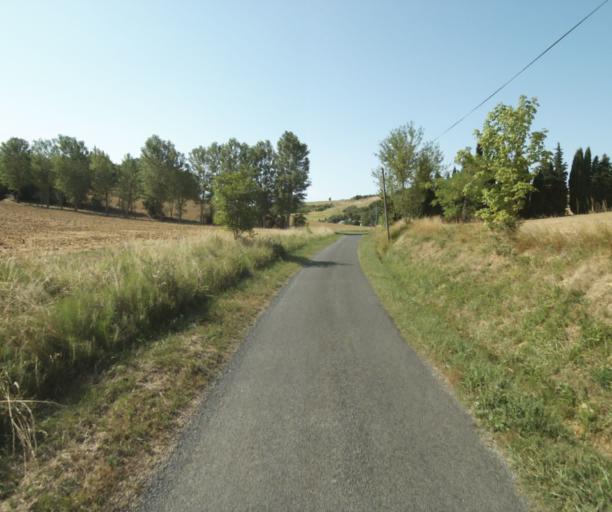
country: FR
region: Midi-Pyrenees
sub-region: Departement de la Haute-Garonne
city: Saint-Felix-Lauragais
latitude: 43.4331
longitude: 1.8469
